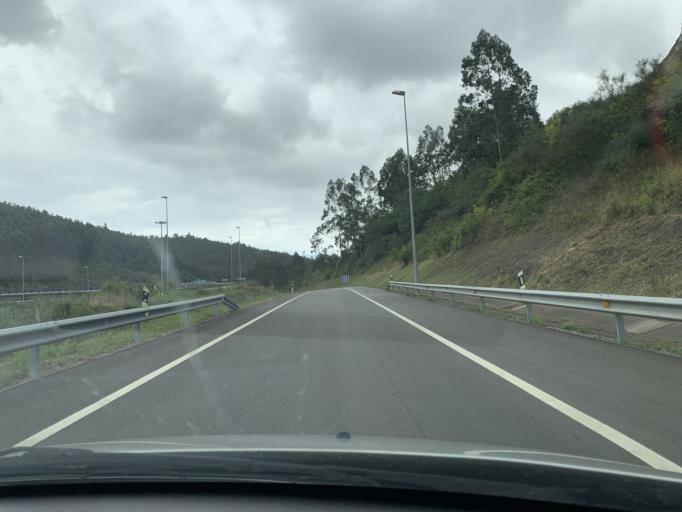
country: ES
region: Asturias
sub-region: Province of Asturias
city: Ribadesella
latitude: 43.4365
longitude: -5.0444
